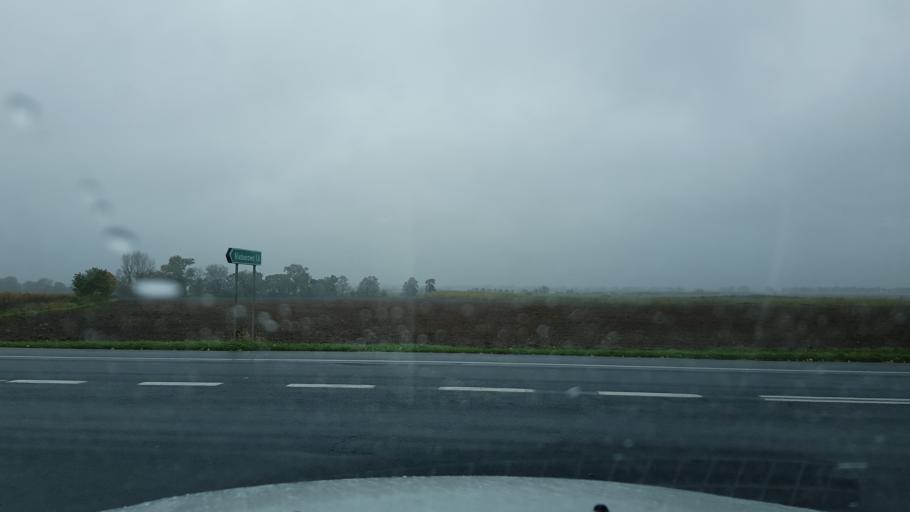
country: PL
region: West Pomeranian Voivodeship
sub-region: Powiat gryfinski
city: Stare Czarnowo
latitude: 53.2109
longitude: 14.8064
